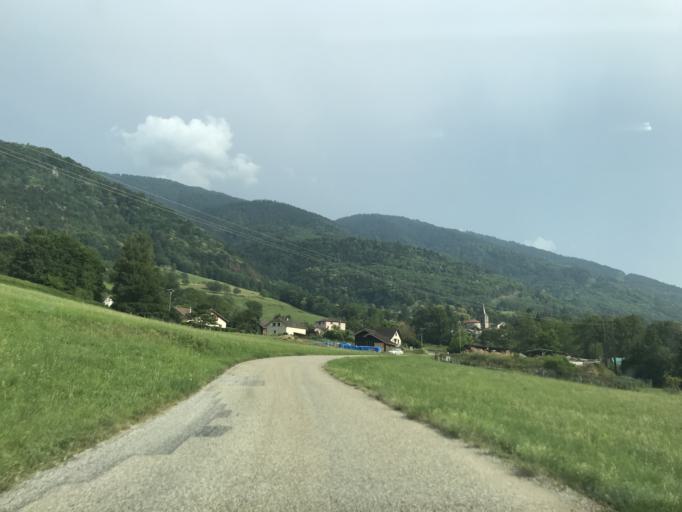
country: FR
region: Rhone-Alpes
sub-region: Departement de l'Isere
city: Allevard
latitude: 45.4274
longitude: 6.0946
